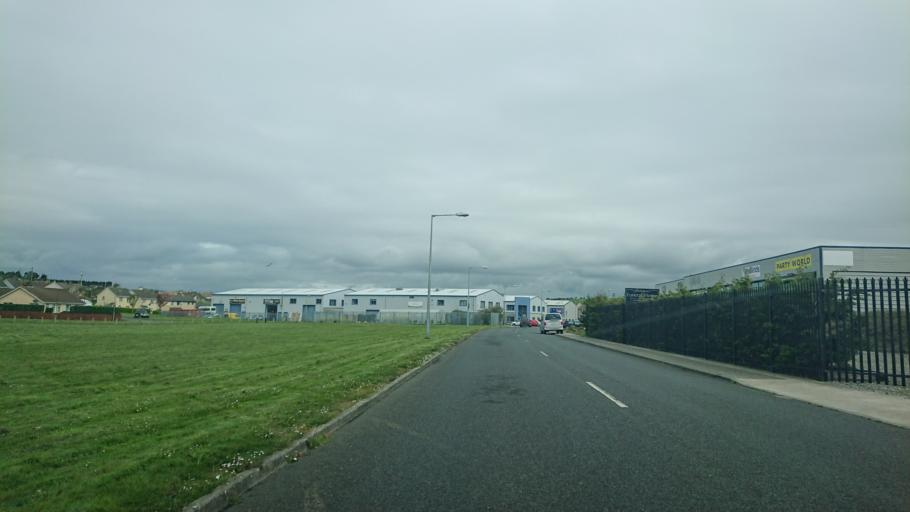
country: IE
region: Munster
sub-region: Waterford
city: Tra Mhor
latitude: 52.1667
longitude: -7.1366
